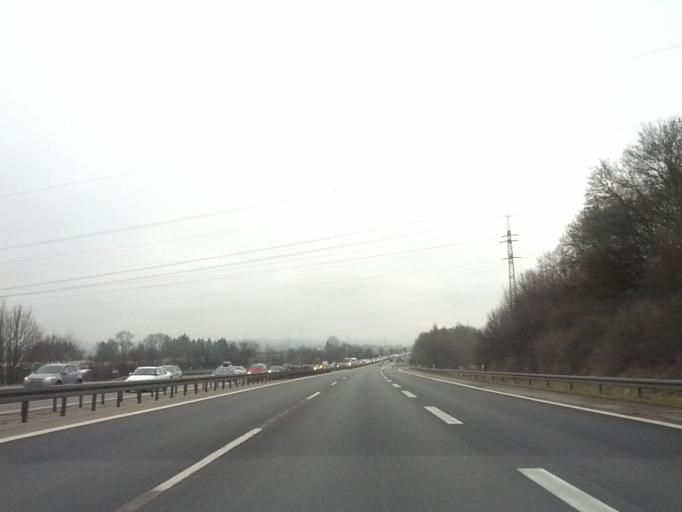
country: DE
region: Bavaria
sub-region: Swabia
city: Memmingen
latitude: 47.9646
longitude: 10.1814
